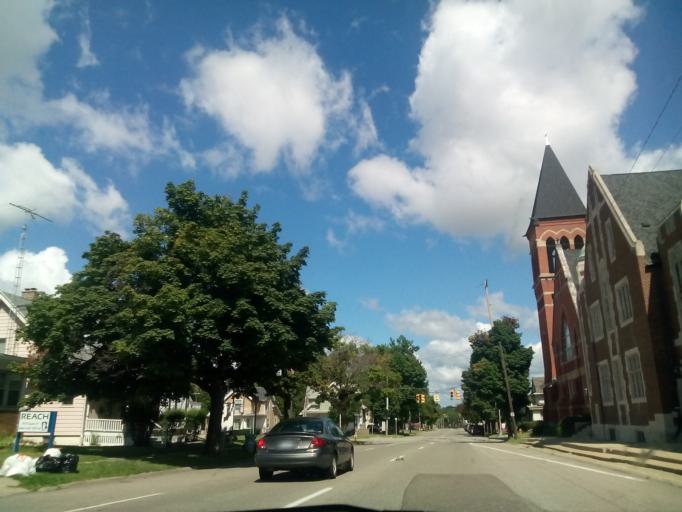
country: US
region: Michigan
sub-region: Genesee County
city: Flint
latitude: 43.0108
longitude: -83.6898
